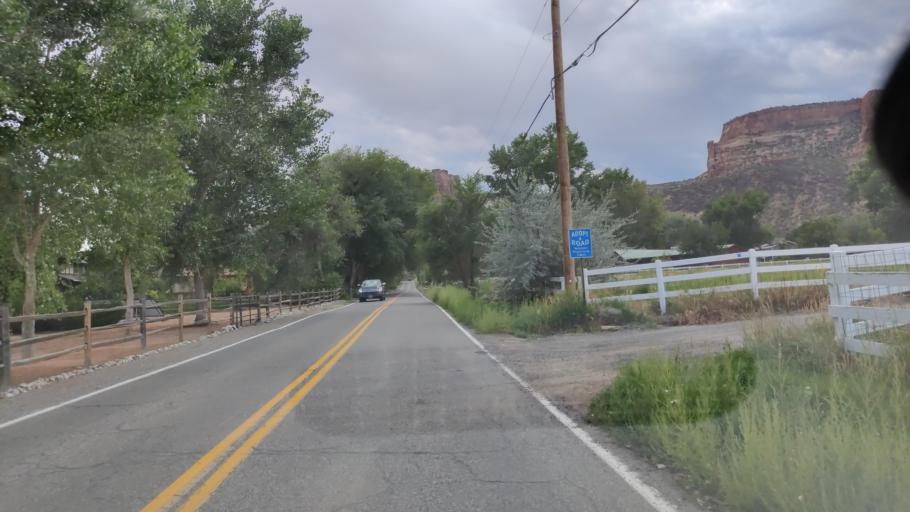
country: US
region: Colorado
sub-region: Mesa County
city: Redlands
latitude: 39.0993
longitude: -108.6920
